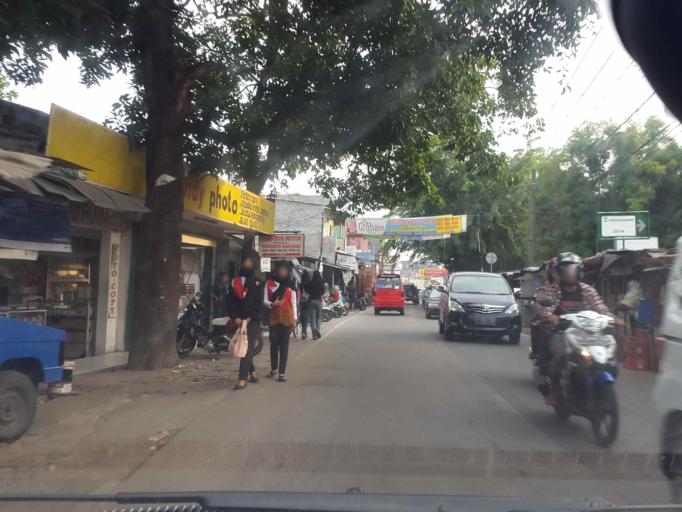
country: ID
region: Banten
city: South Tangerang
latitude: -6.2714
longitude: 106.7431
